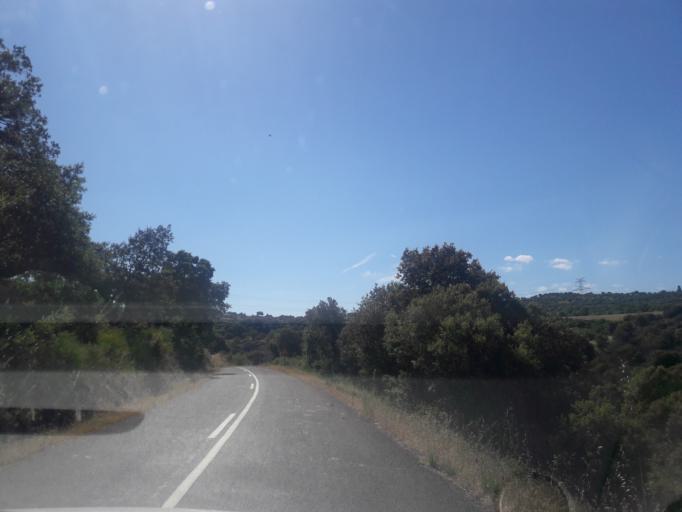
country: ES
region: Castille and Leon
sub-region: Provincia de Salamanca
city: Saucelle
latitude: 41.0077
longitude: -6.7371
